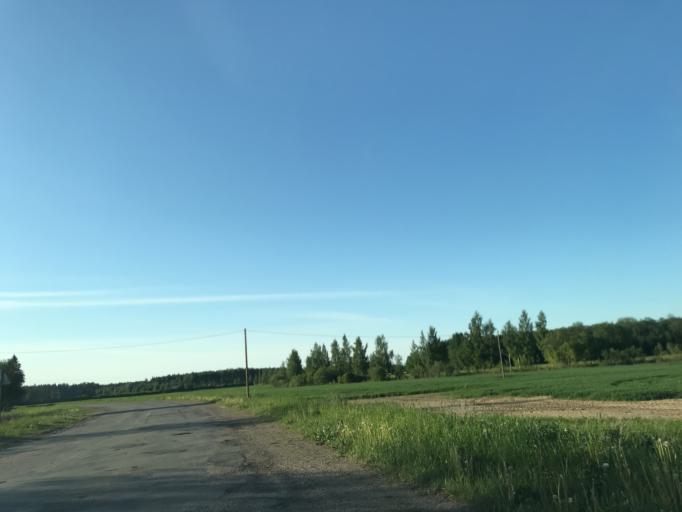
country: LV
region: Ozolnieku
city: Ozolnieki
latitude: 56.5788
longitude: 23.8265
